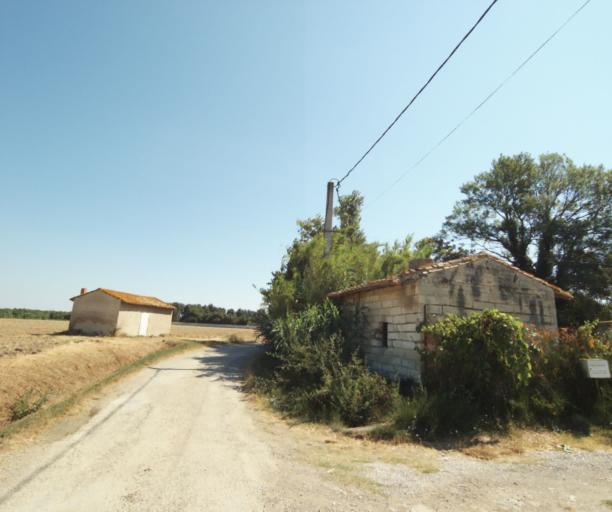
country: FR
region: Languedoc-Roussillon
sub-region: Departement de l'Herault
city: Marsillargues
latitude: 43.6383
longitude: 4.1526
